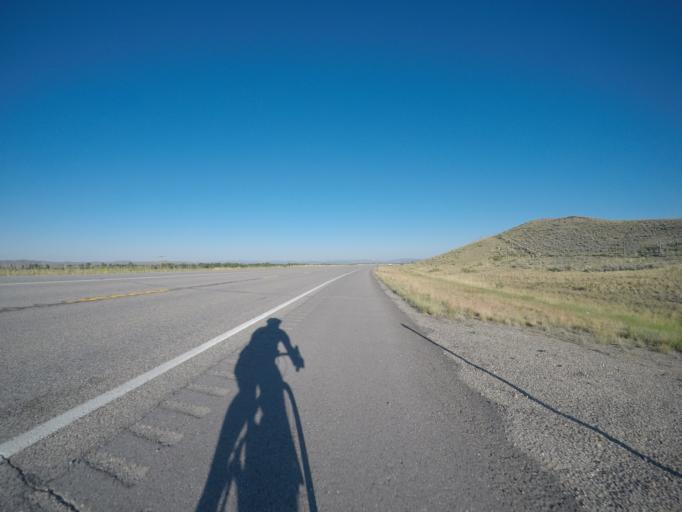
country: US
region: Wyoming
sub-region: Sublette County
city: Pinedale
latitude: 42.8814
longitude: -109.9928
